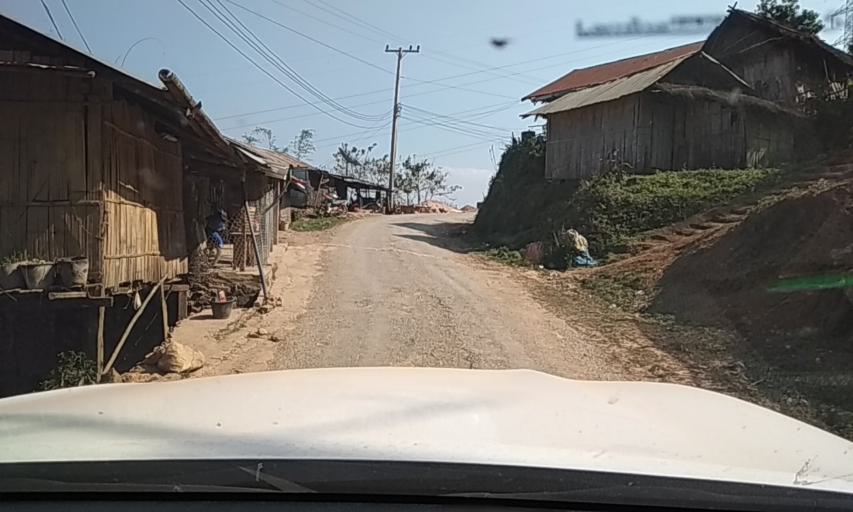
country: LA
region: Phongsali
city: Phongsali
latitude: 21.6603
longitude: 102.0914
